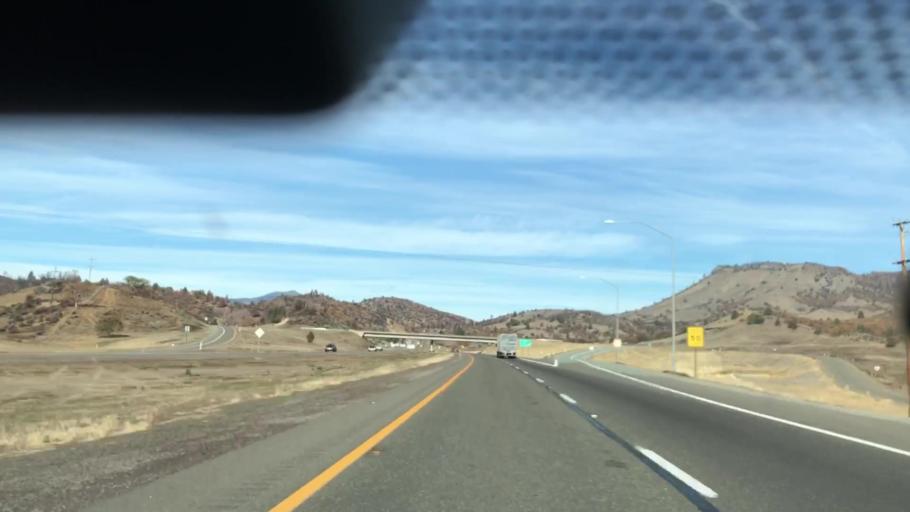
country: US
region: California
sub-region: Siskiyou County
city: Yreka
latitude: 41.9508
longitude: -122.5900
